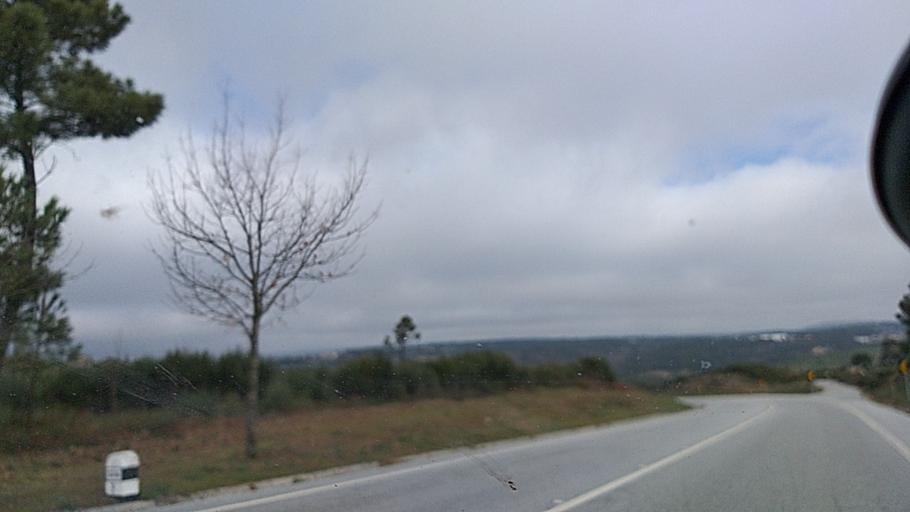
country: PT
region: Guarda
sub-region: Aguiar da Beira
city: Aguiar da Beira
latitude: 40.7699
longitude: -7.5033
